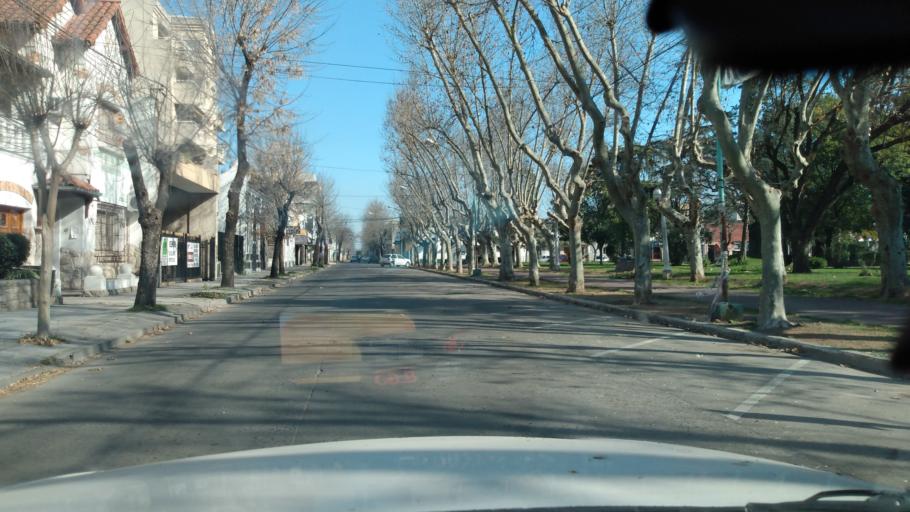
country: AR
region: Buenos Aires
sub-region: Partido de Lujan
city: Lujan
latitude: -34.5663
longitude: -59.1139
